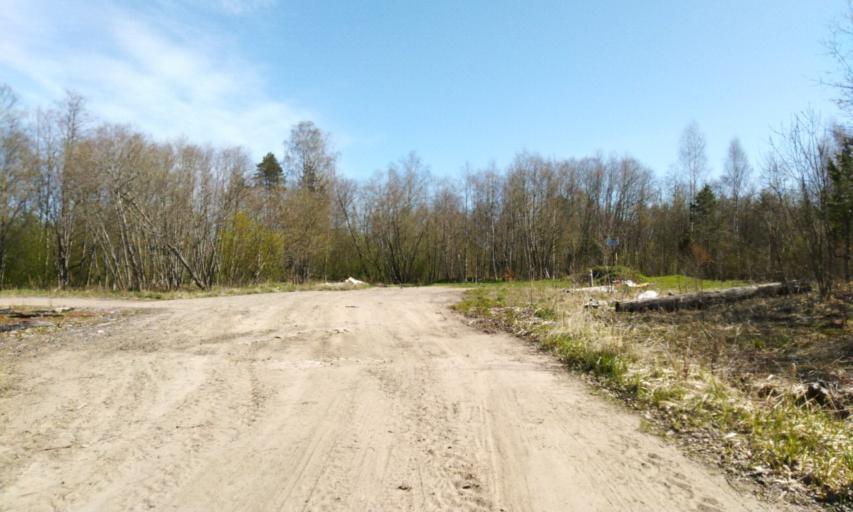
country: RU
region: Leningrad
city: Garbolovo
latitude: 60.4217
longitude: 30.4698
